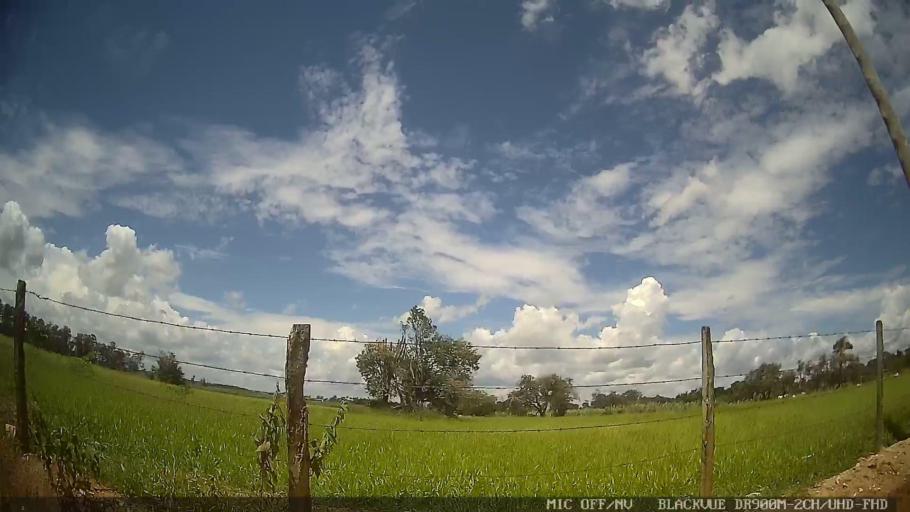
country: BR
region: Sao Paulo
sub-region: Conchas
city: Conchas
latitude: -23.0650
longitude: -47.9778
